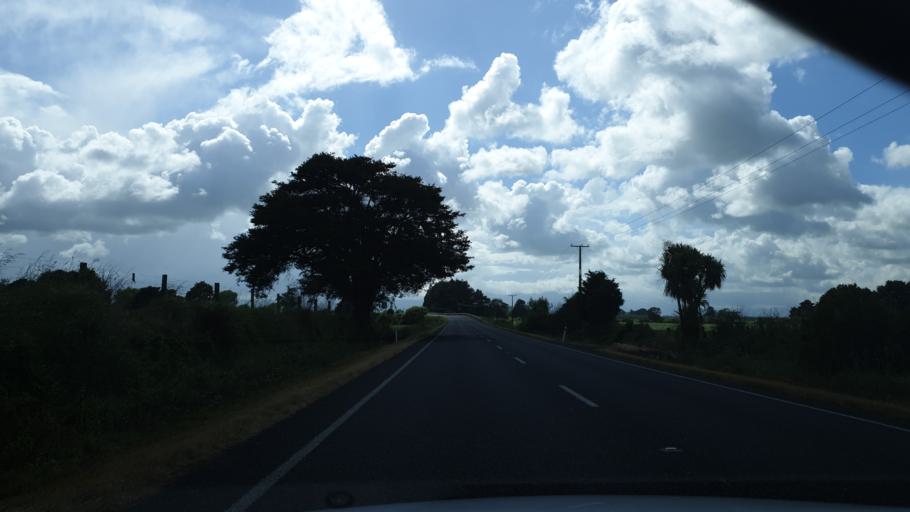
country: NZ
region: Waikato
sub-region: Hauraki District
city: Paeroa
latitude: -37.5144
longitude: 175.5017
